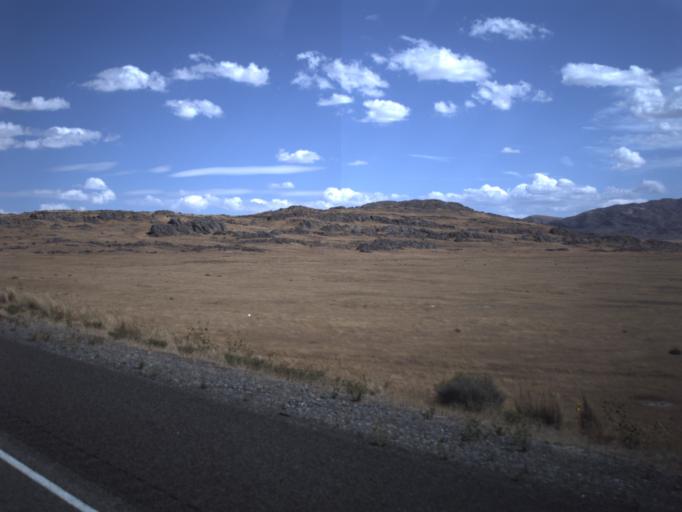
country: US
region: Utah
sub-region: Tooele County
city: Grantsville
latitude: 40.7553
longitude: -113.0271
